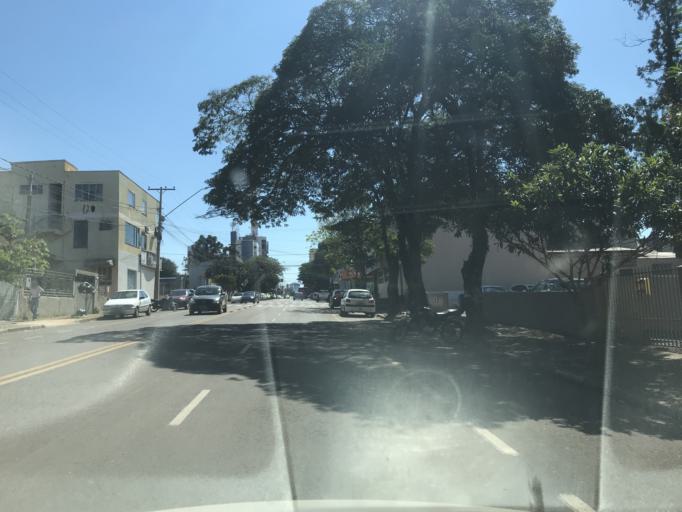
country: BR
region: Parana
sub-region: Toledo
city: Toledo
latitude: -24.7360
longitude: -53.7421
